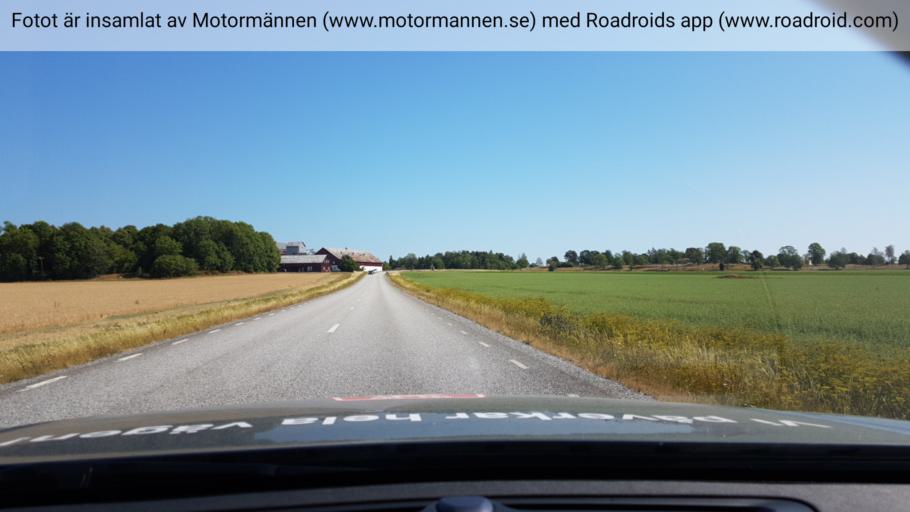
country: SE
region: Stockholm
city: Stenhamra
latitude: 59.3963
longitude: 17.5462
